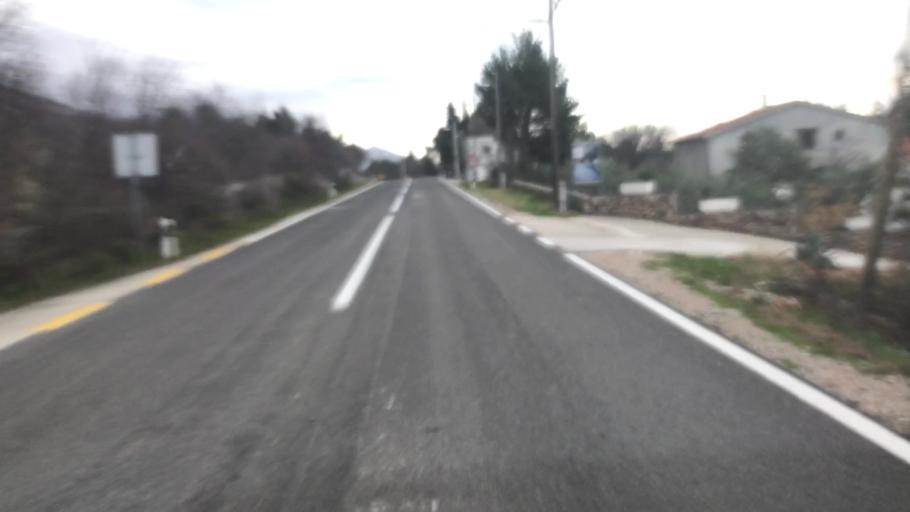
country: HR
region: Zadarska
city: Razanac
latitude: 44.3371
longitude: 15.3445
